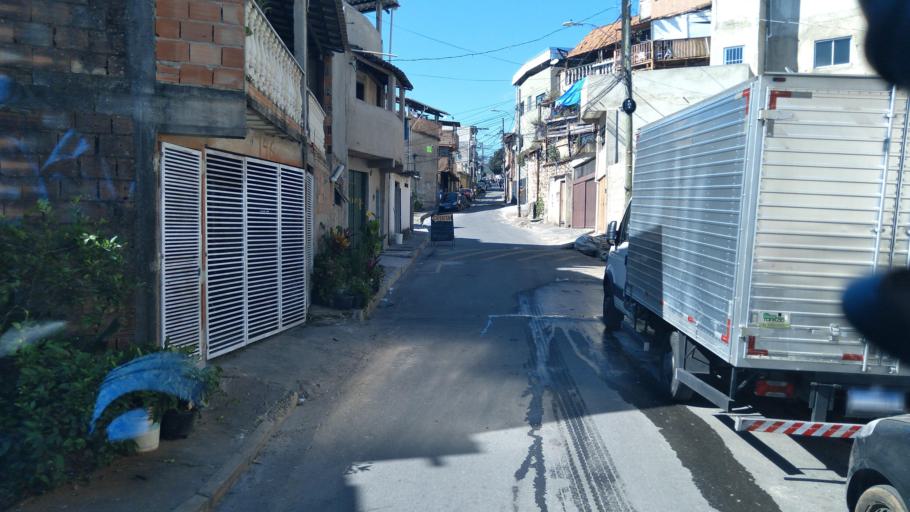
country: BR
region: Minas Gerais
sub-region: Belo Horizonte
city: Belo Horizonte
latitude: -19.9069
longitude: -43.8901
